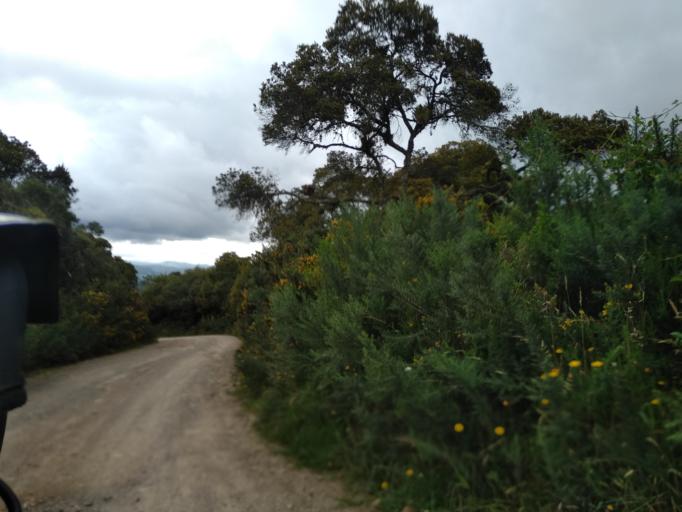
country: CO
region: Boyaca
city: Sotaquira
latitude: 5.7531
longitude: -73.2939
